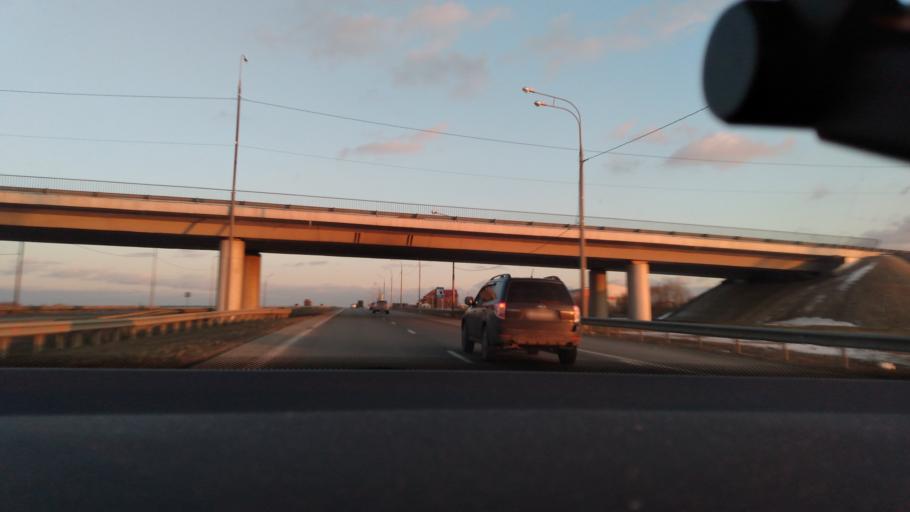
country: RU
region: Moskovskaya
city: Kolomna
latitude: 55.1211
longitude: 38.8175
